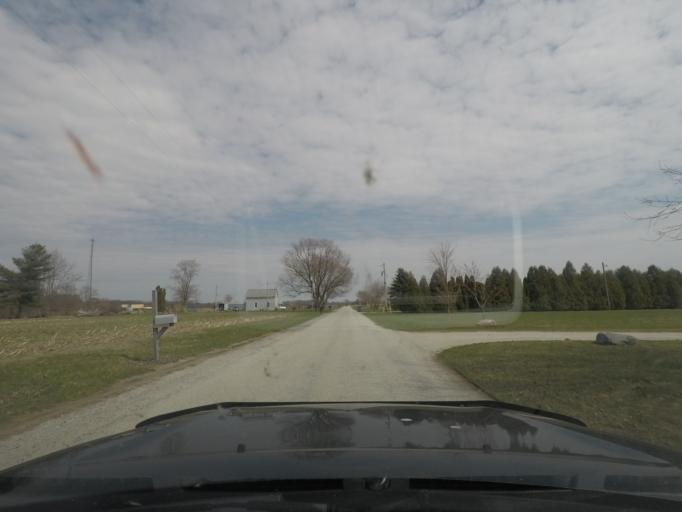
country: US
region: Indiana
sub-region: LaPorte County
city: Kingsford Heights
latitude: 41.4728
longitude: -86.6717
